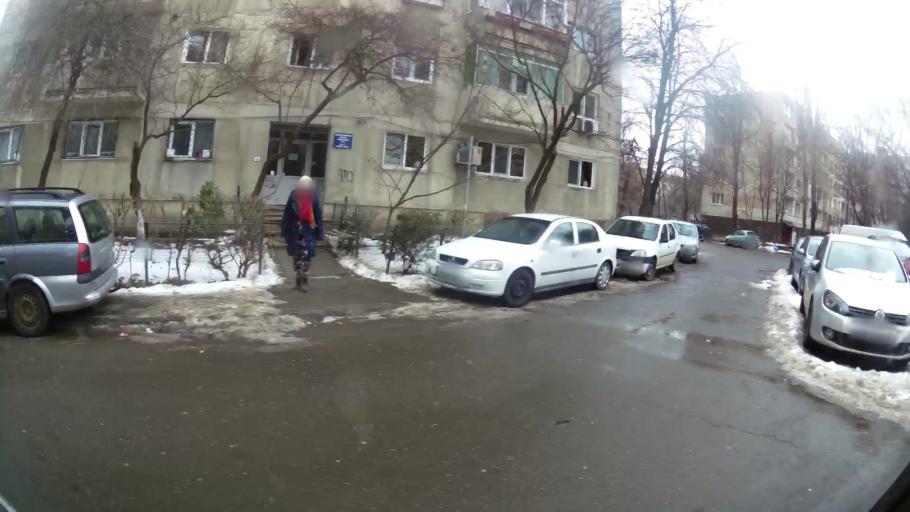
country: RO
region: Ilfov
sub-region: Comuna Chiajna
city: Rosu
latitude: 44.4218
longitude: 26.0240
